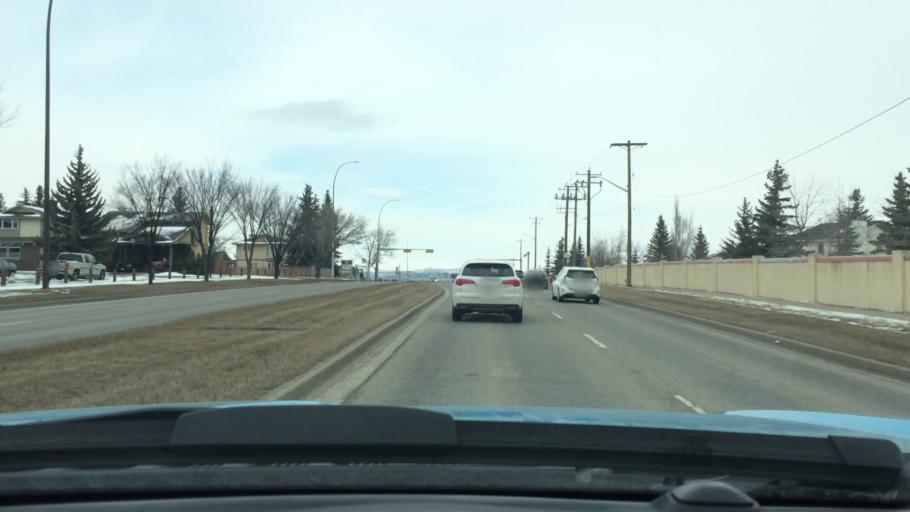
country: CA
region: Alberta
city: Calgary
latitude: 51.1334
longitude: -114.1067
